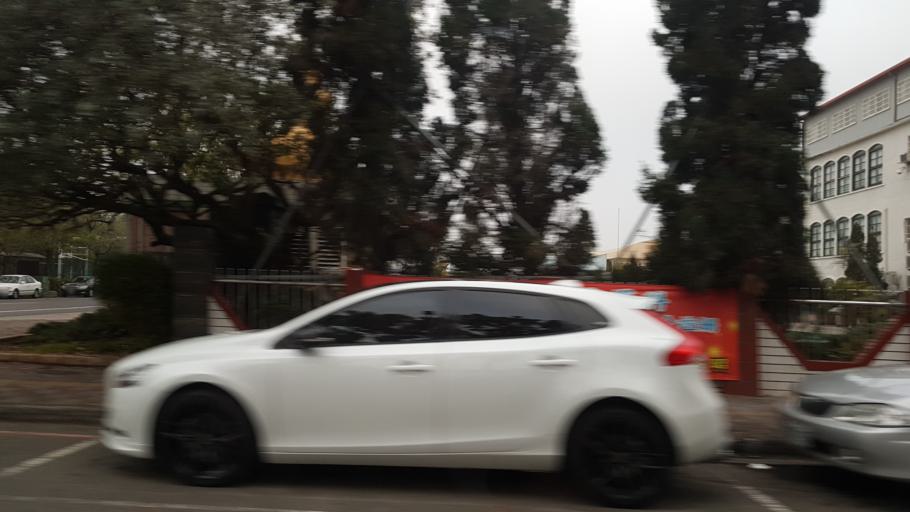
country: TW
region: Taiwan
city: Xinying
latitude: 23.3159
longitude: 120.3121
